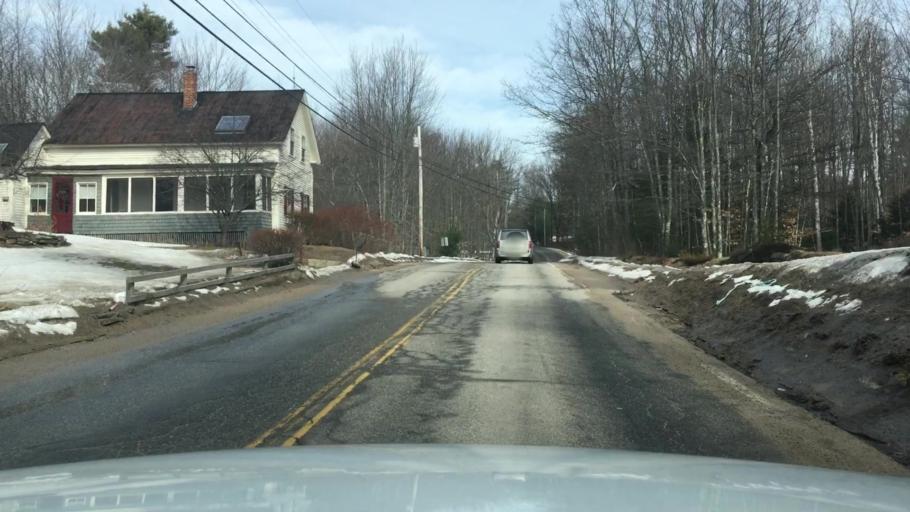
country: US
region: Maine
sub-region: York County
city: Springvale
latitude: 43.4879
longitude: -70.8076
